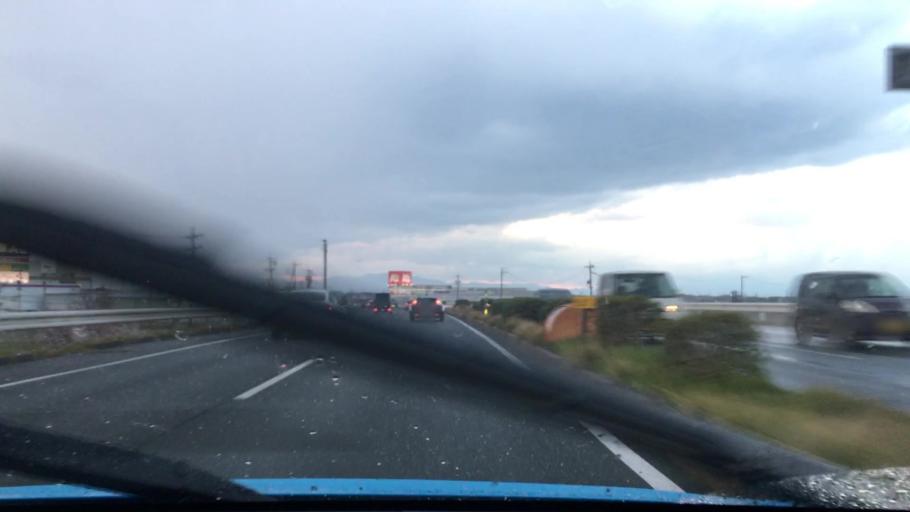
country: JP
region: Mie
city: Ise
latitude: 34.5795
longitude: 136.6209
